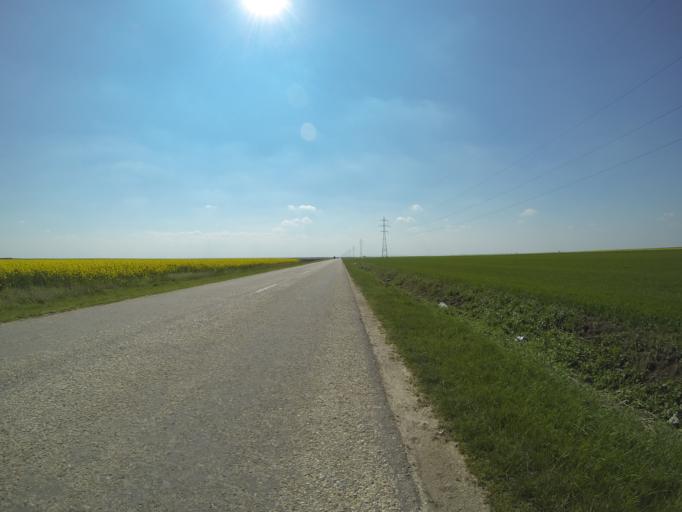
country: RO
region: Dolj
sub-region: Comuna Unirea
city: Unirea
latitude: 44.1648
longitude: 23.1594
